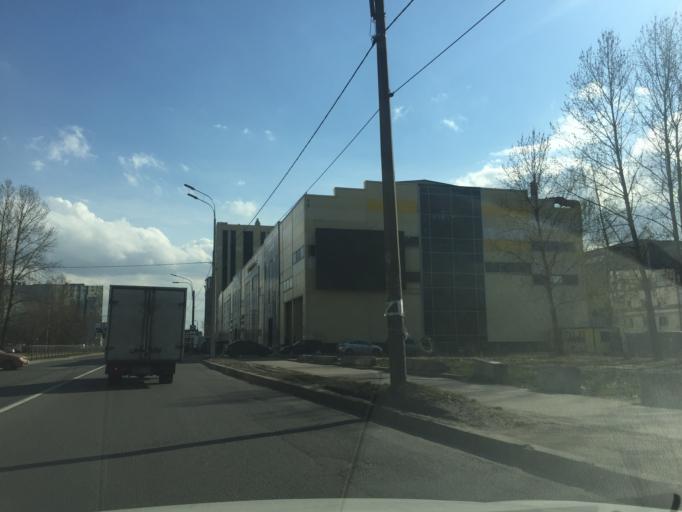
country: RU
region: St.-Petersburg
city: Krasnogvargeisky
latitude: 59.9390
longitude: 30.4351
